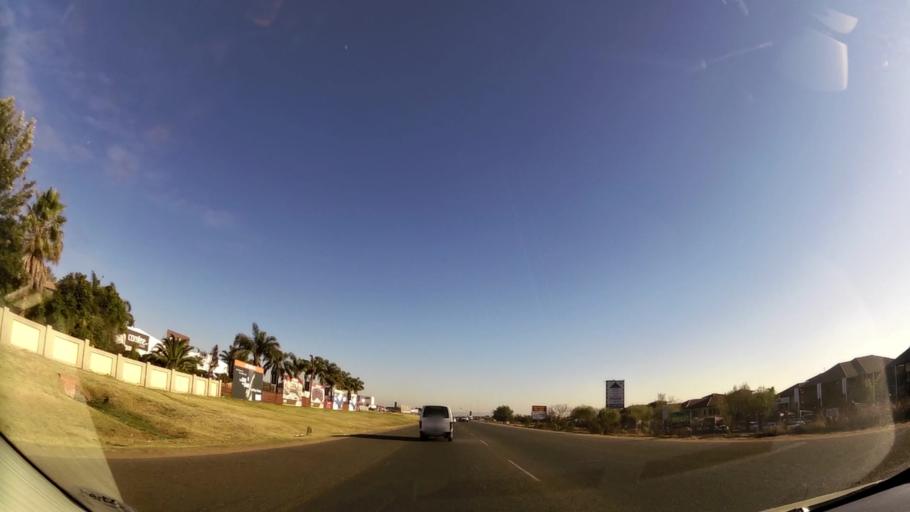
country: ZA
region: Gauteng
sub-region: City of Johannesburg Metropolitan Municipality
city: Roodepoort
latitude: -26.1001
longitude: 27.8769
